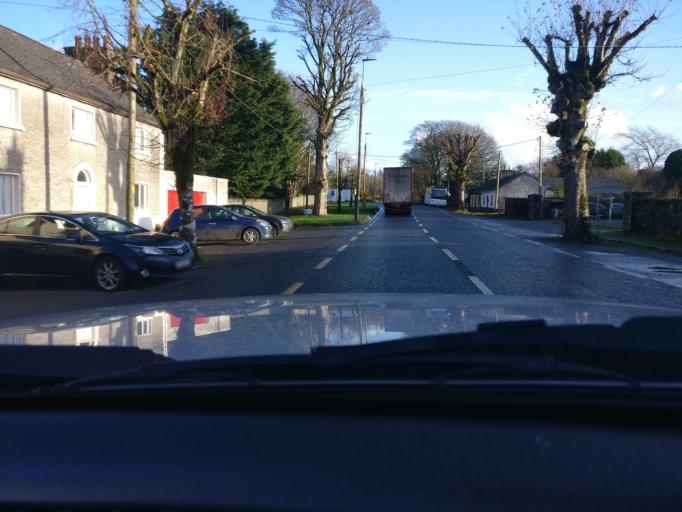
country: IE
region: Leinster
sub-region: An Mhi
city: Athboy
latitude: 53.6631
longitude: -7.0123
